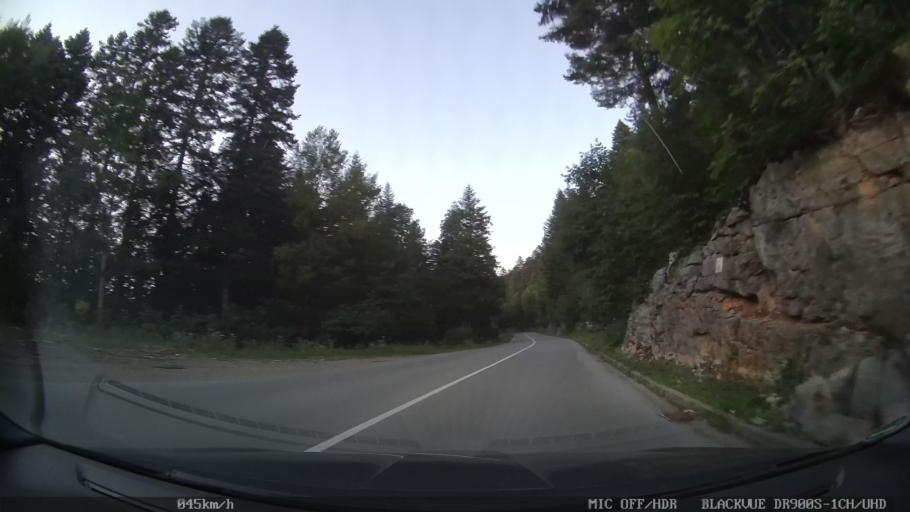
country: HR
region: Primorsko-Goranska
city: Novi Vinodolski
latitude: 45.1783
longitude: 14.9275
